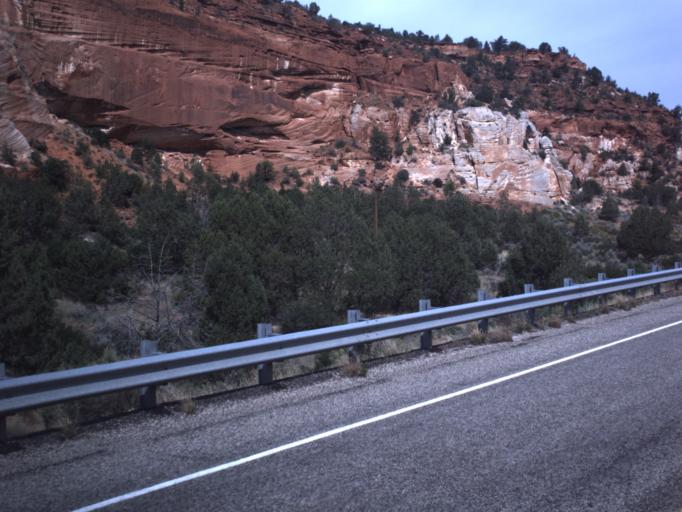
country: US
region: Utah
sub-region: Kane County
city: Kanab
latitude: 37.1052
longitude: -112.5489
